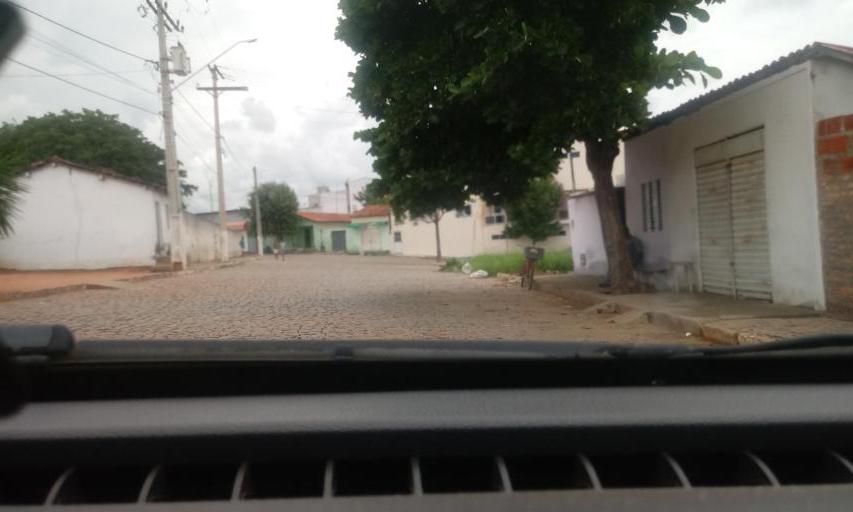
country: BR
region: Bahia
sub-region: Riacho De Santana
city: Riacho de Santana
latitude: -13.9124
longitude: -42.8476
